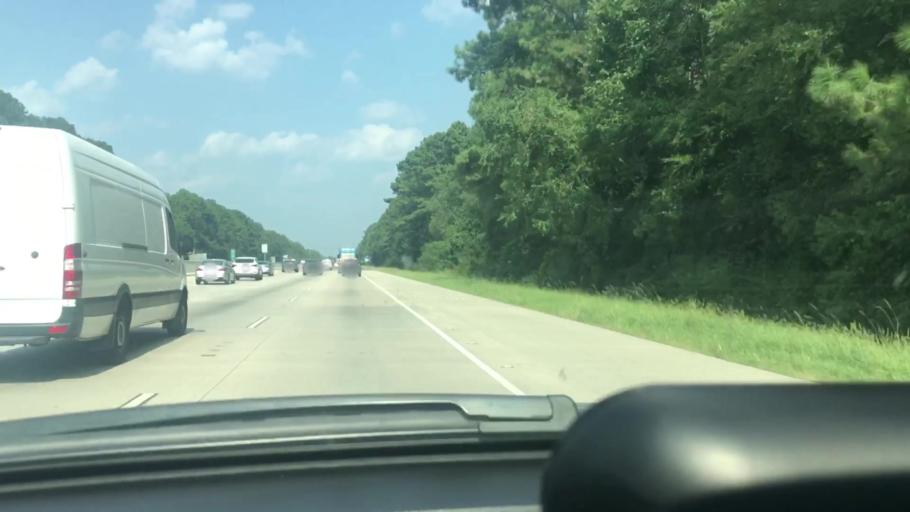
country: US
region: Louisiana
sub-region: Livingston Parish
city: Denham Springs
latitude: 30.4578
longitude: -90.9448
